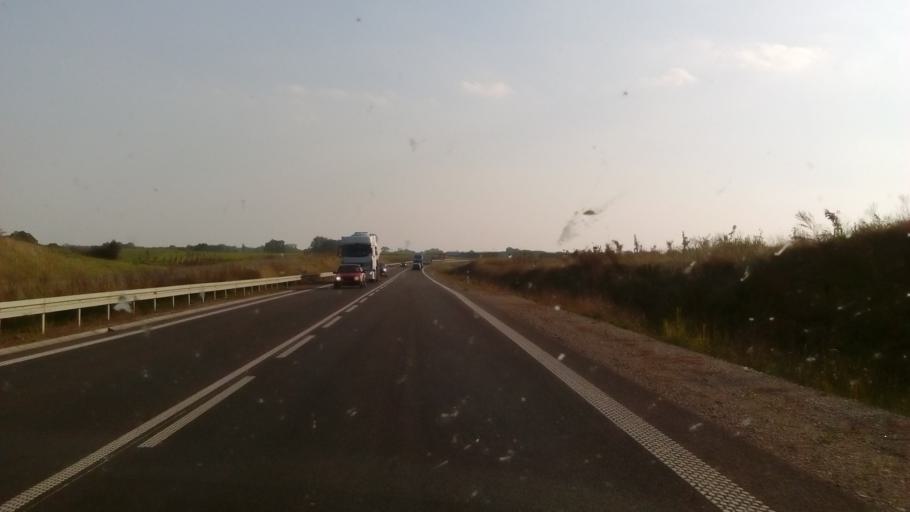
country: PL
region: Podlasie
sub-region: Powiat grajewski
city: Rajgrod
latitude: 53.7725
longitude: 22.8340
